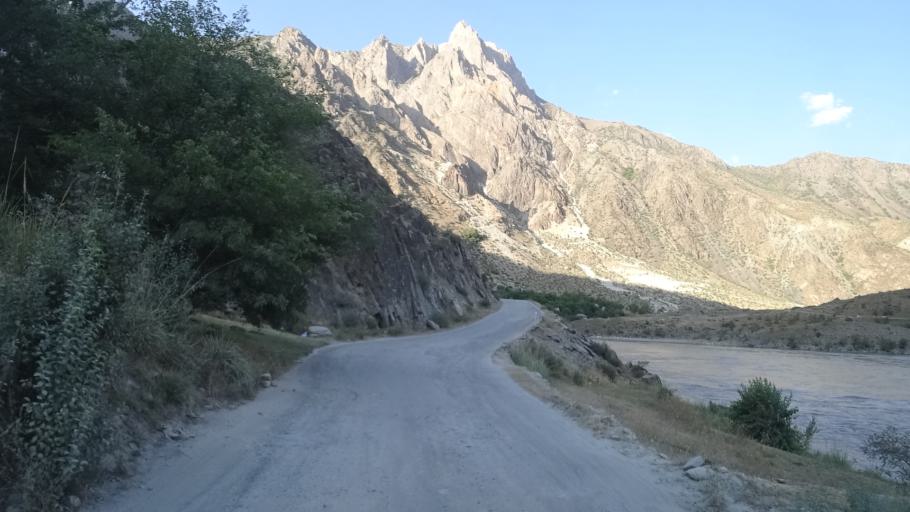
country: AF
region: Badakhshan
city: Maymay
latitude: 38.4899
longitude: 70.9864
